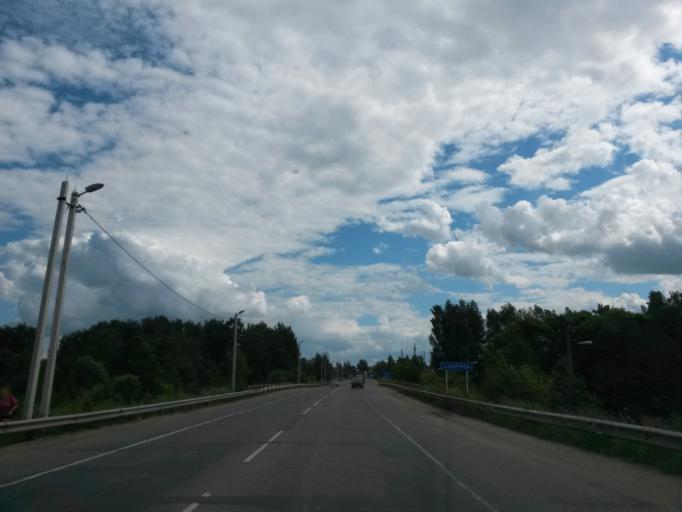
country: RU
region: Ivanovo
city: Novo-Talitsy
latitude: 57.0090
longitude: 40.8401
